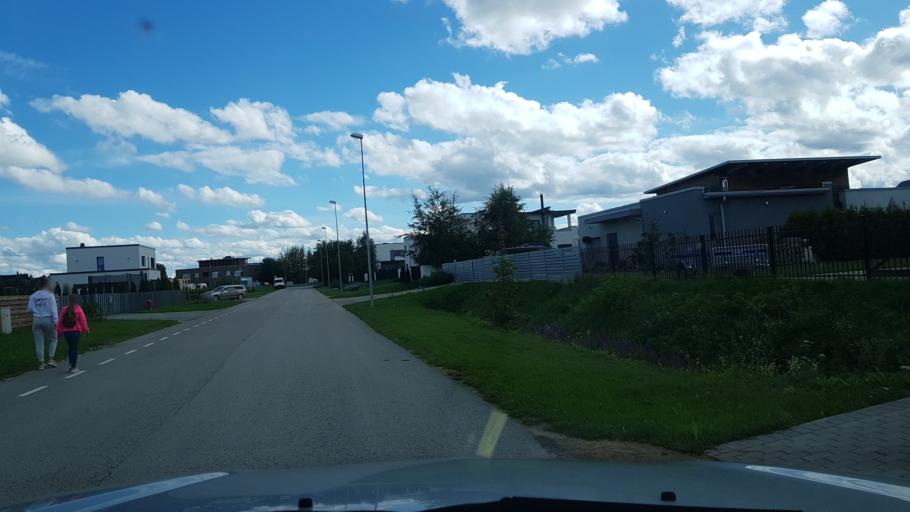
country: EE
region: Harju
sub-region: Tallinna linn
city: Tallinn
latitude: 59.3941
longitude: 24.7980
